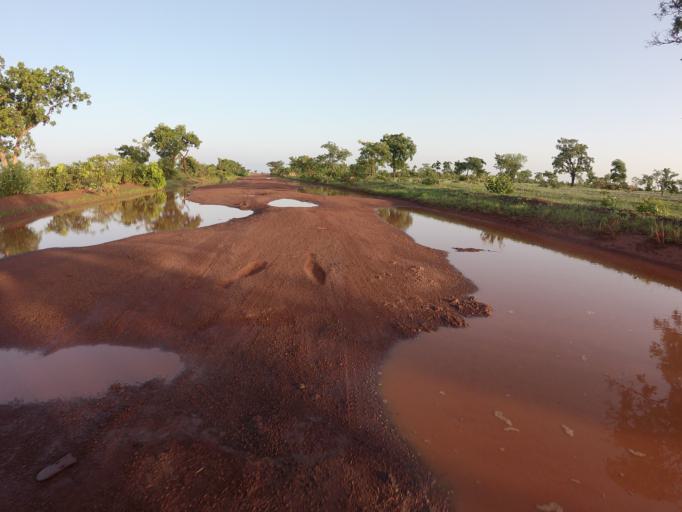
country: TG
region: Savanes
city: Sansanne-Mango
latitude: 10.2354
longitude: -0.0741
